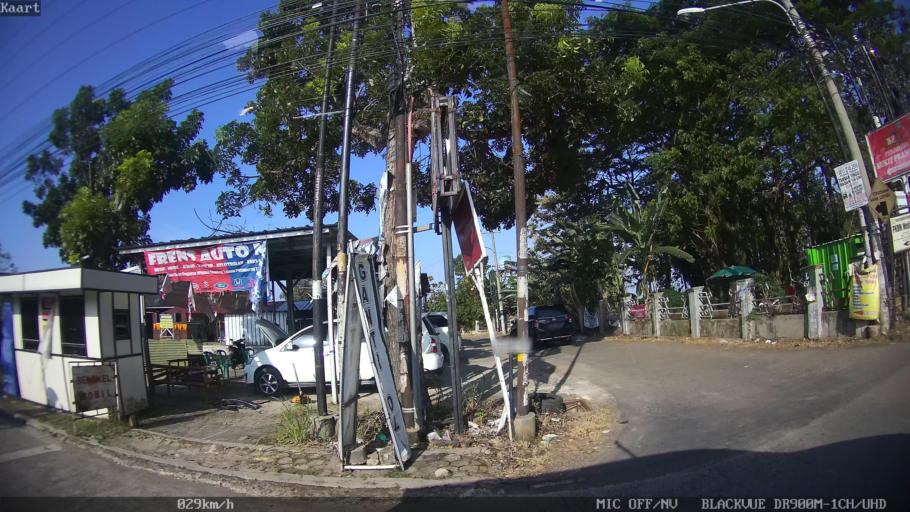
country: ID
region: Lampung
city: Kedaton
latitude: -5.3827
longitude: 105.2216
